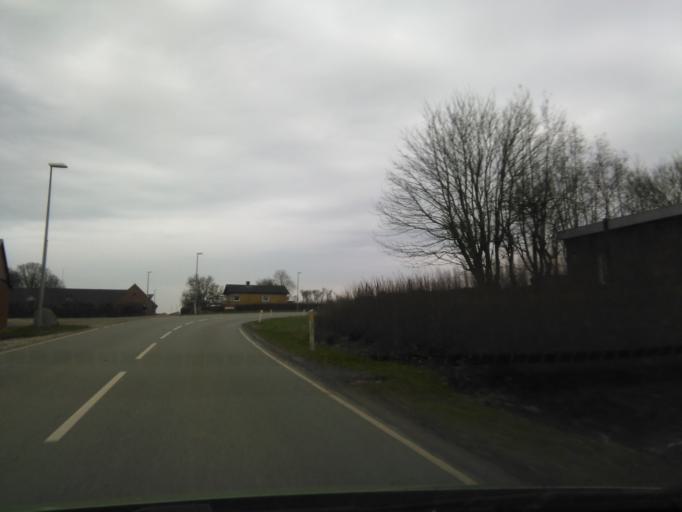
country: DK
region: Central Jutland
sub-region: Randers Kommune
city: Spentrup
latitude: 56.5206
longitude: 10.0114
